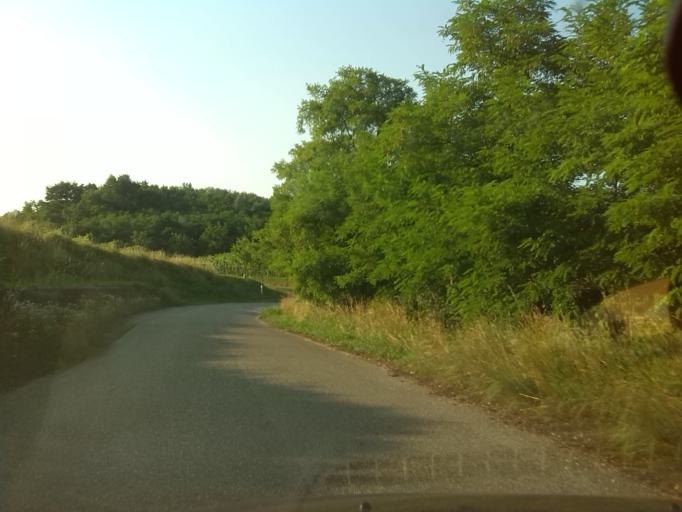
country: IT
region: Friuli Venezia Giulia
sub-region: Provincia di Gorizia
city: Cormons
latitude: 45.9848
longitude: 13.4799
